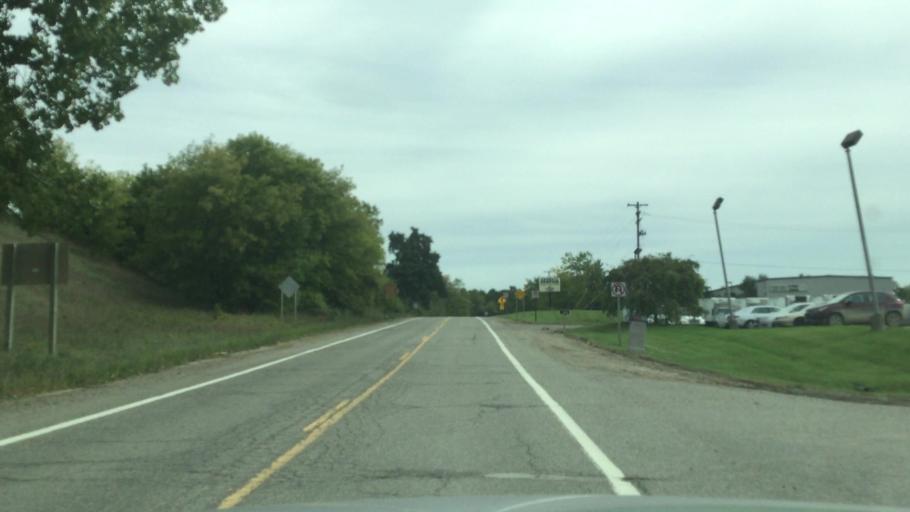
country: US
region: Michigan
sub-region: Oakland County
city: Holly
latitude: 42.8156
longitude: -83.5657
